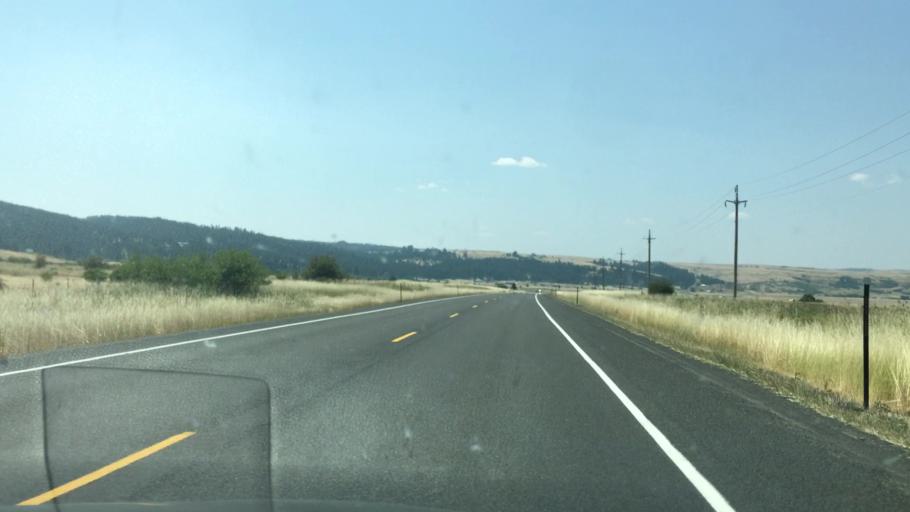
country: US
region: Idaho
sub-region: Idaho County
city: Grangeville
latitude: 45.8973
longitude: -116.1840
